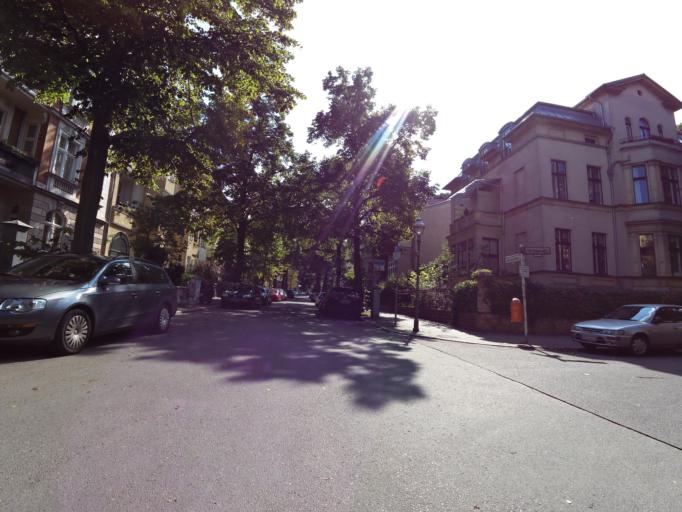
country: DE
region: Berlin
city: Schoneberg Bezirk
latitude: 52.4715
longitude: 13.3403
